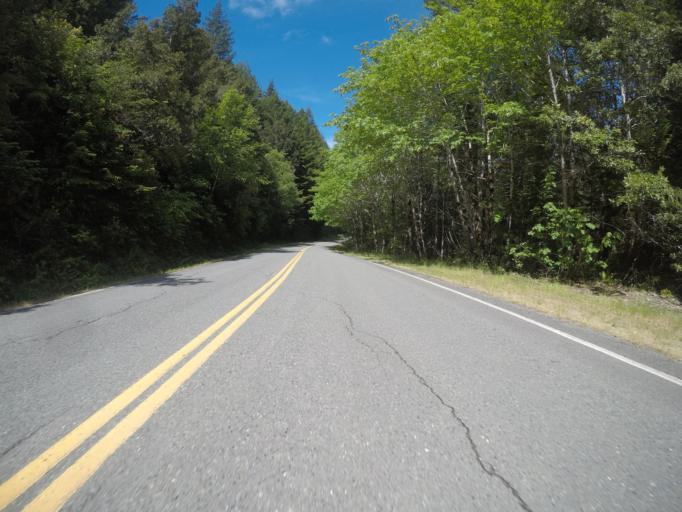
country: US
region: California
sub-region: Del Norte County
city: Bertsch-Oceanview
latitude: 41.7264
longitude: -123.9589
